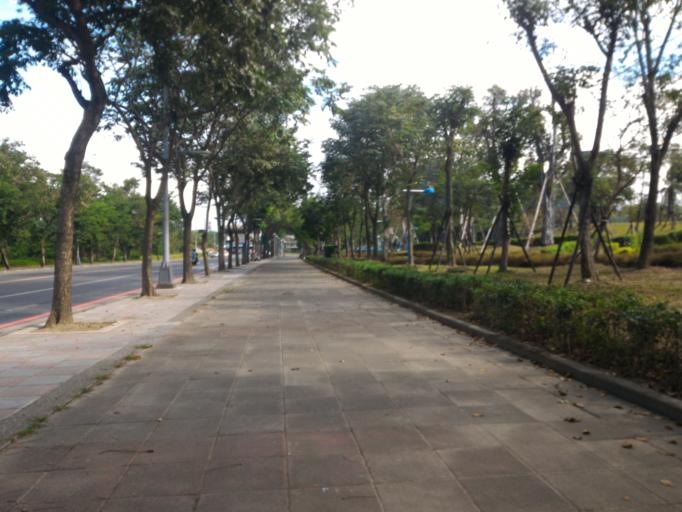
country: TW
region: Taiwan
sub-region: Taoyuan
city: Taoyuan
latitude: 24.9512
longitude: 121.3851
